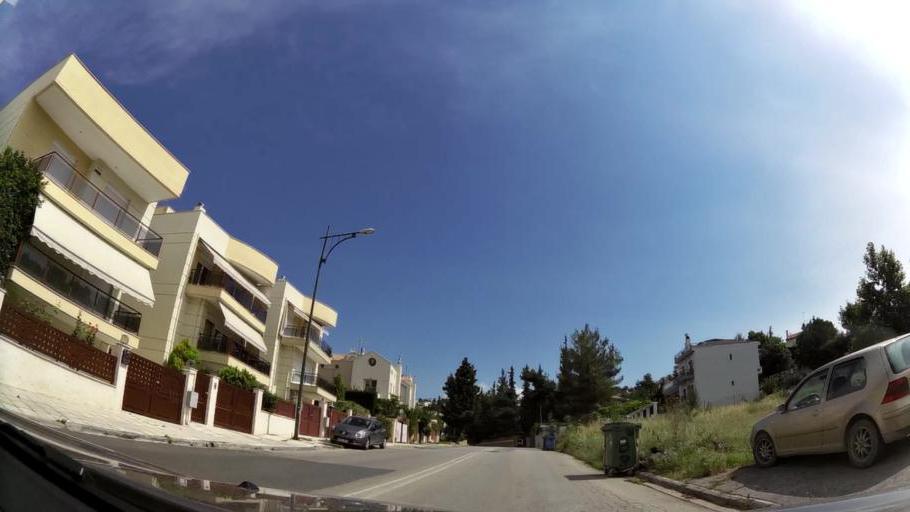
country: GR
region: Central Macedonia
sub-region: Nomos Thessalonikis
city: Panorama
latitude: 40.5830
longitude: 23.0223
